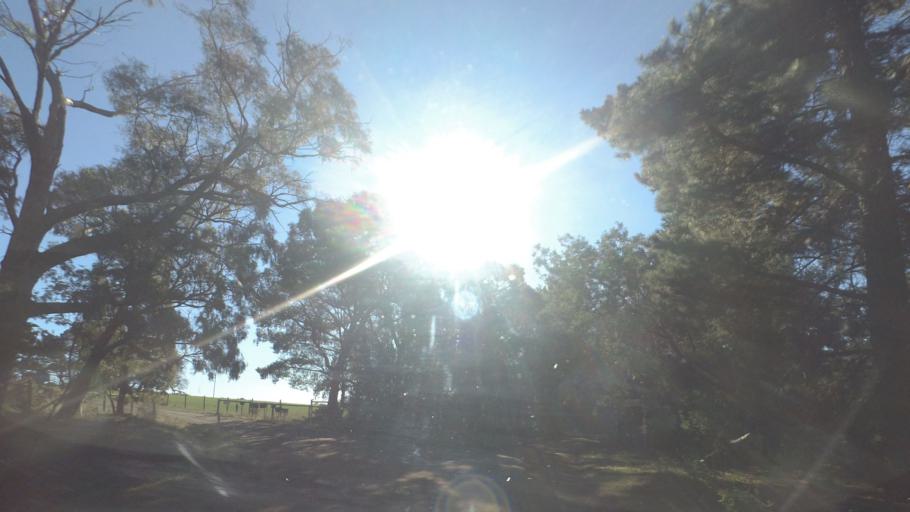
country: AU
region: Victoria
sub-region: Mount Alexander
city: Castlemaine
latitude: -37.2721
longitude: 144.3365
